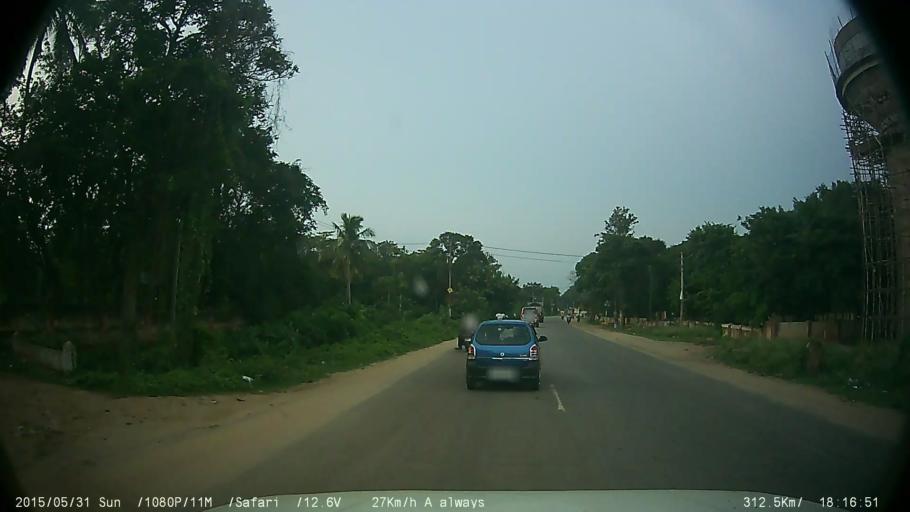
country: IN
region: Karnataka
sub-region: Mysore
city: Nanjangud
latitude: 12.1163
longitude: 76.6740
